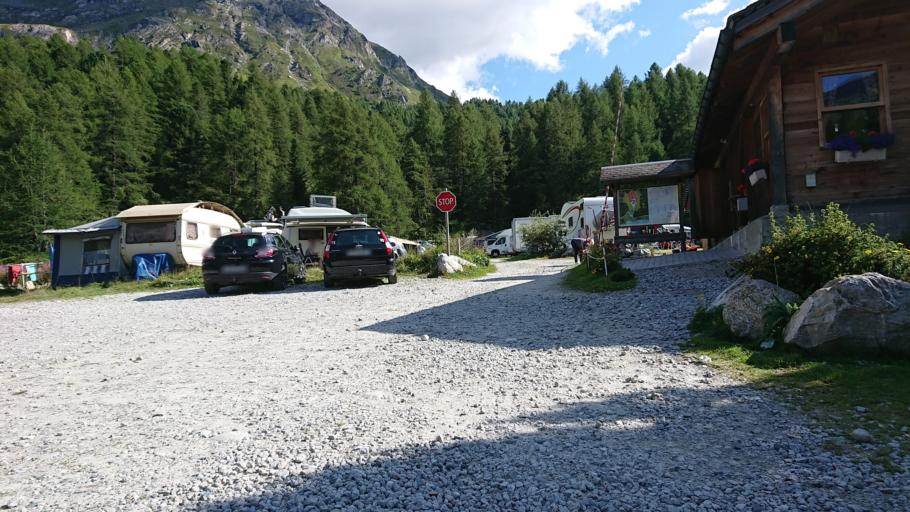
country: CH
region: Grisons
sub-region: Maloja District
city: Silvaplana
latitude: 46.4059
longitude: 9.7106
